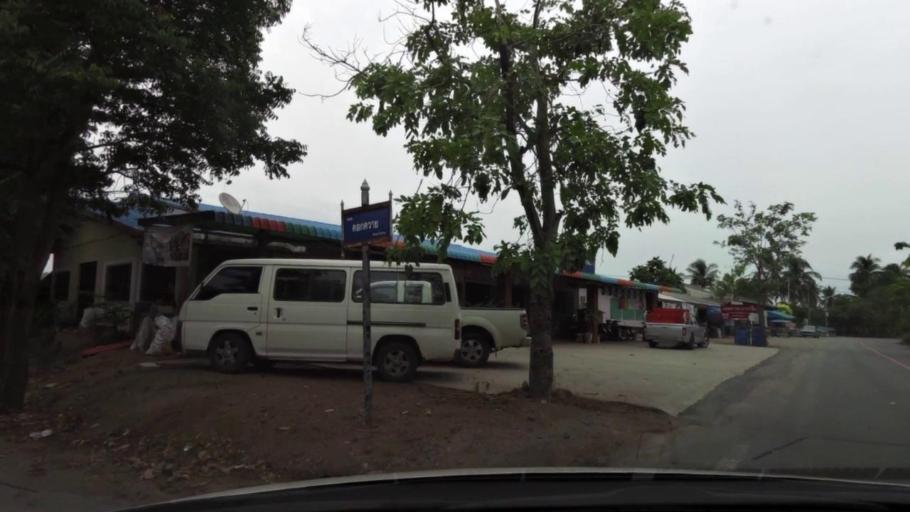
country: TH
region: Samut Sakhon
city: Ban Phaeo
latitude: 13.5987
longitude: 100.0251
